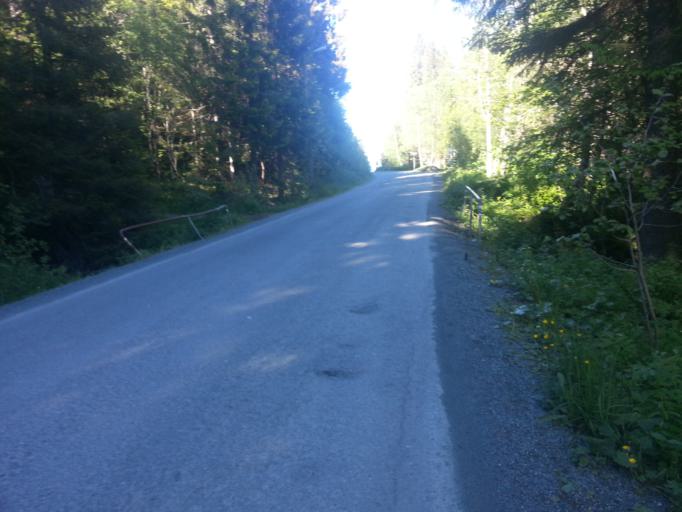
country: NO
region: Sor-Trondelag
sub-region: Trondheim
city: Trondheim
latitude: 63.4243
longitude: 10.3395
